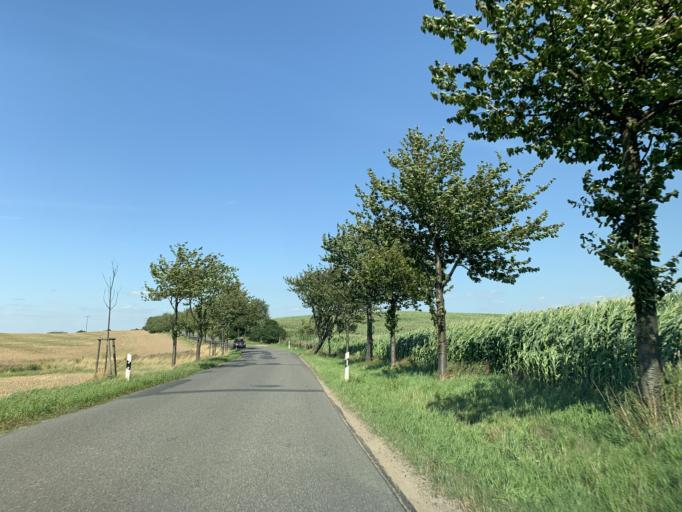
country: DE
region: Mecklenburg-Vorpommern
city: Loitz
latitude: 53.3422
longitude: 13.3903
